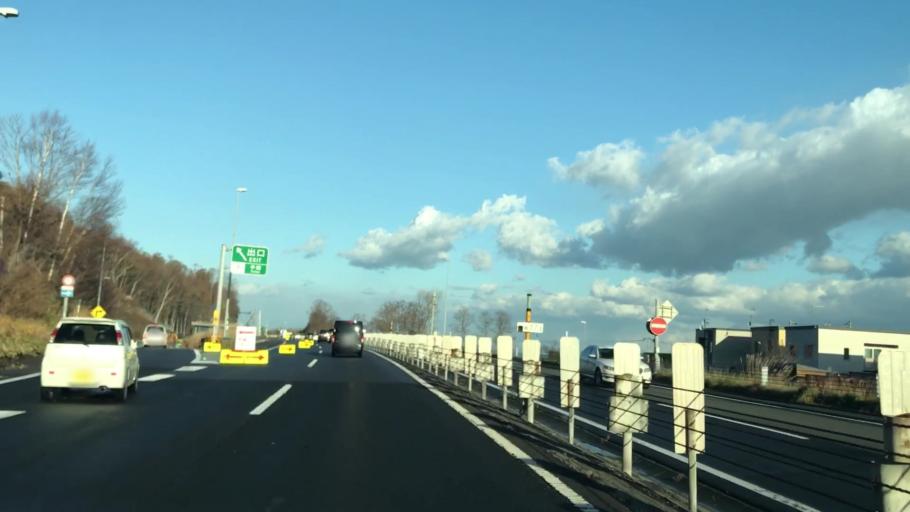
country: JP
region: Hokkaido
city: Sapporo
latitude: 43.1097
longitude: 141.2407
